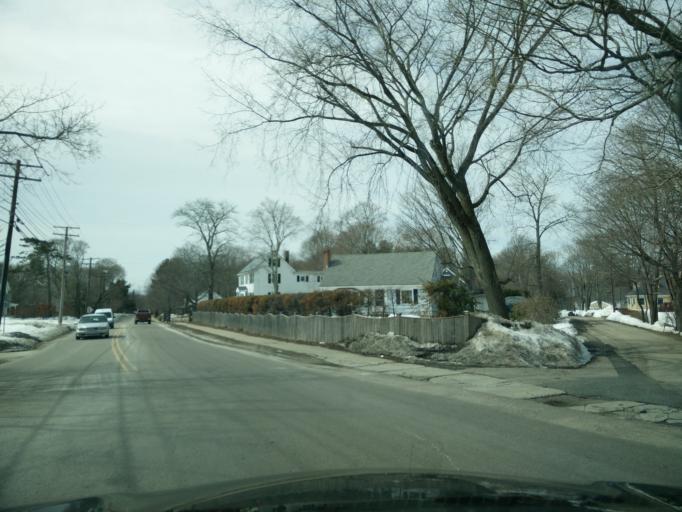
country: US
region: Massachusetts
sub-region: Norfolk County
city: Walpole
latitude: 42.1479
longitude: -71.2365
